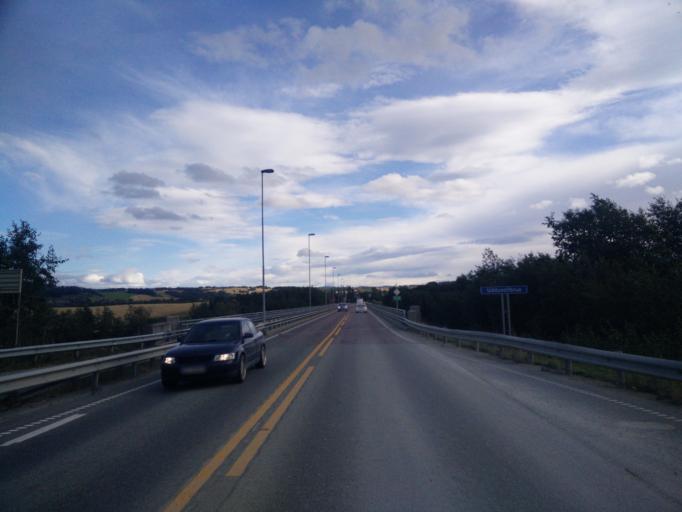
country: NO
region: Sor-Trondelag
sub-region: Melhus
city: Melhus
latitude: 63.3228
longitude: 10.2702
